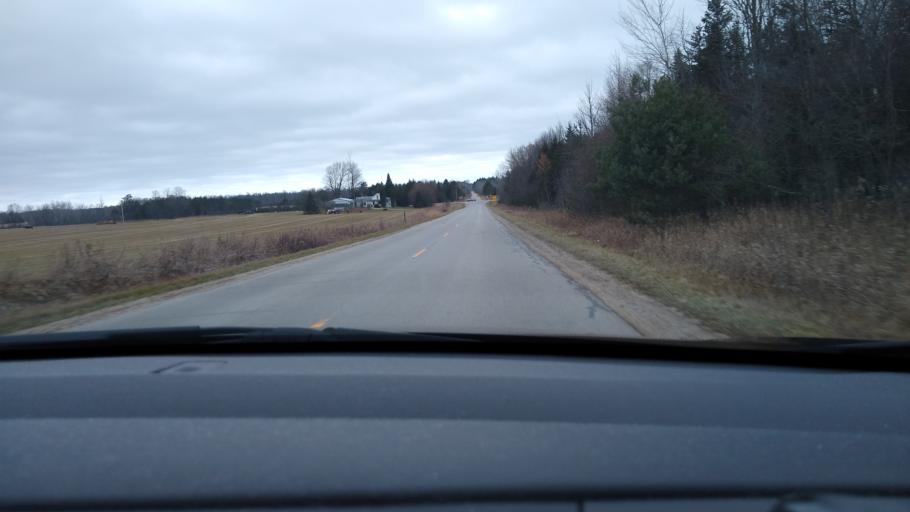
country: US
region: Michigan
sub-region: Missaukee County
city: Lake City
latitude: 44.3340
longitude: -85.0550
